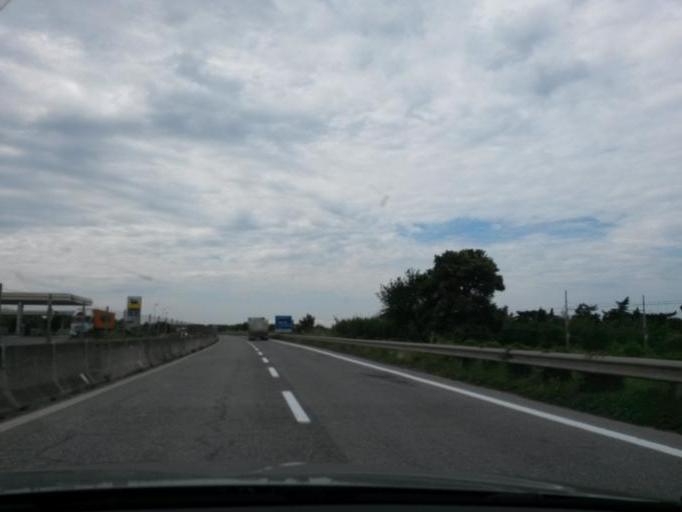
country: IT
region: Tuscany
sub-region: Provincia di Livorno
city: San Vincenzo
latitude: 43.1237
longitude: 10.5456
